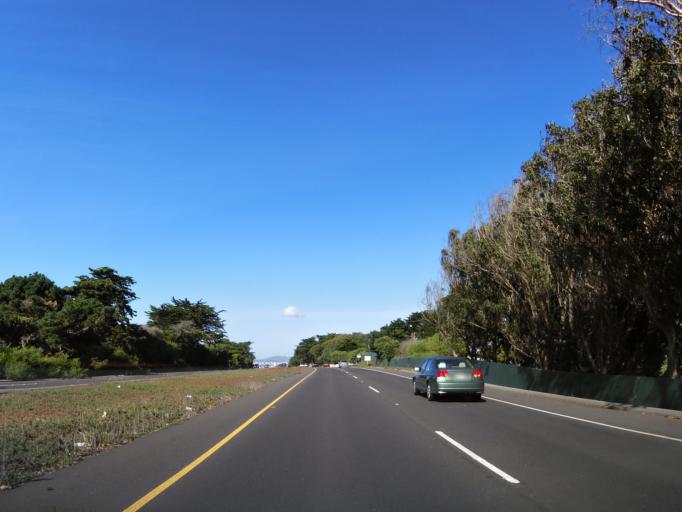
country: US
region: California
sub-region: San Mateo County
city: Broadmoor
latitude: 37.7083
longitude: -122.4981
